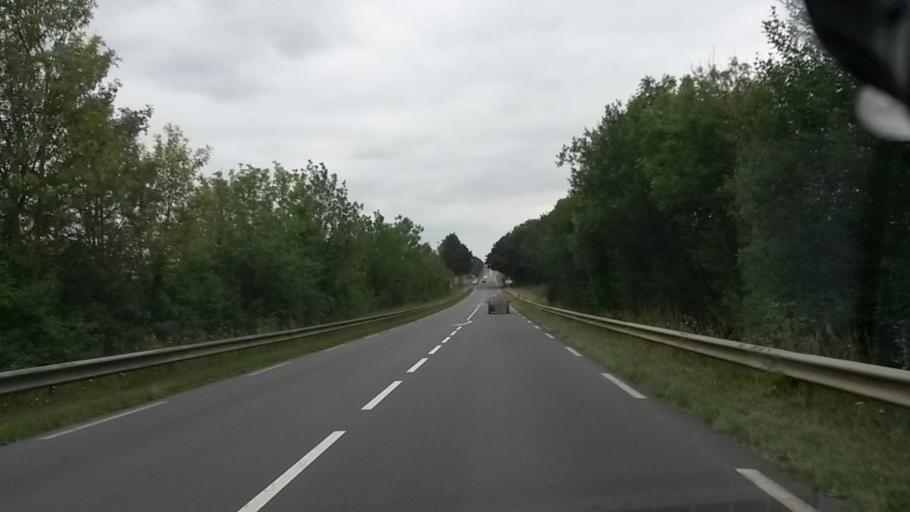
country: FR
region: Picardie
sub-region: Departement de la Somme
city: Albert
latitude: 49.9833
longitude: 2.5854
